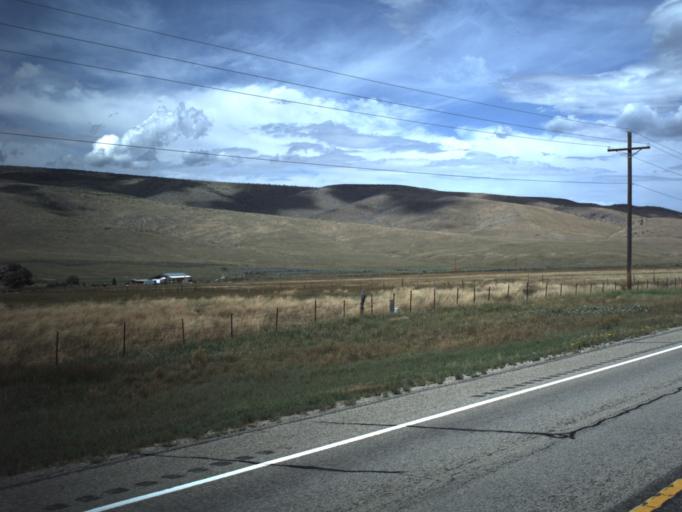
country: US
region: Utah
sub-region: Sanpete County
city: Fairview
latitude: 39.8008
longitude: -111.5013
